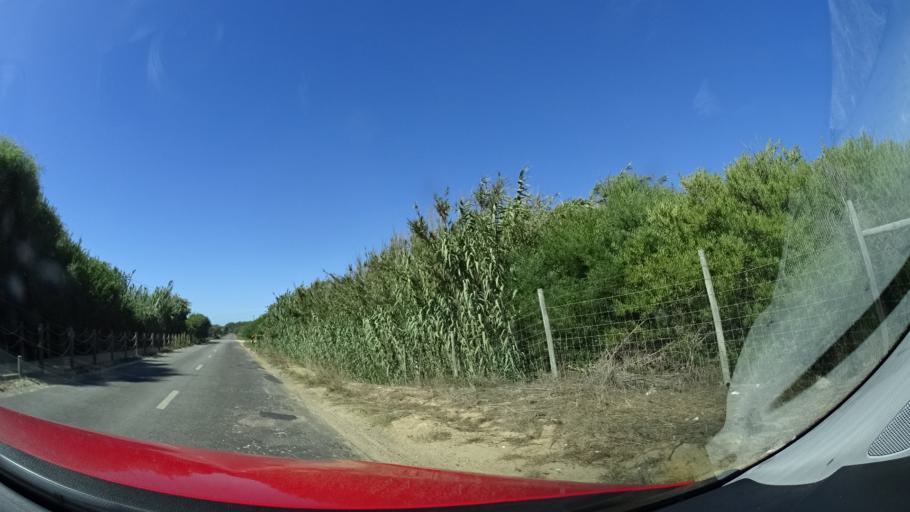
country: PT
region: Beja
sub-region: Odemira
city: Sao Teotonio
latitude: 37.5432
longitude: -8.7879
